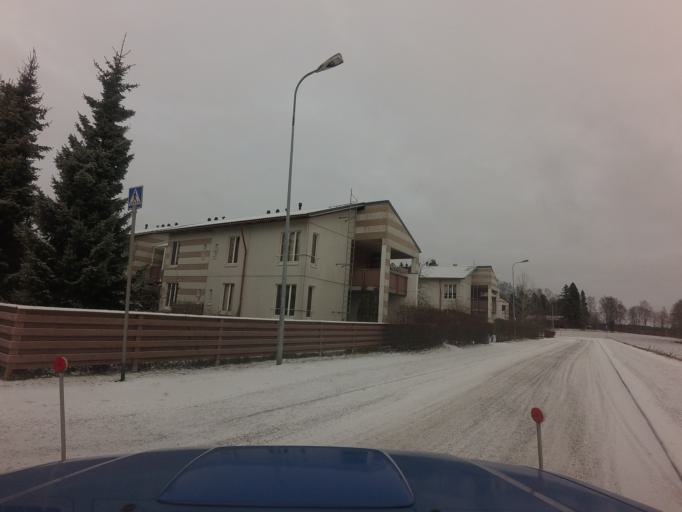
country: FI
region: Uusimaa
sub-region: Helsinki
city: Kilo
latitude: 60.2328
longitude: 24.7840
